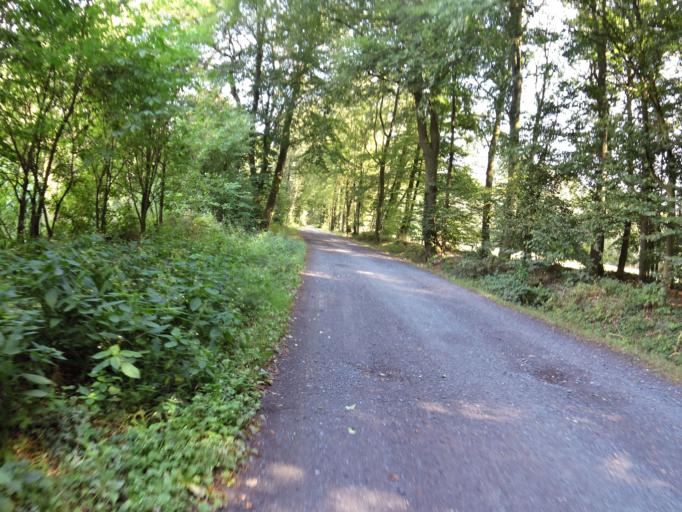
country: DE
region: North Rhine-Westphalia
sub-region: Regierungsbezirk Munster
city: Warendorf
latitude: 51.9376
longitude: 7.9232
